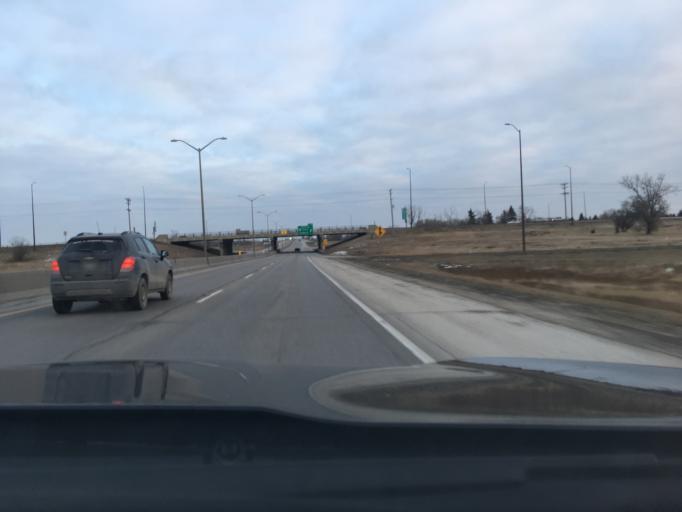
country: CA
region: Manitoba
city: Winnipeg
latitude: 49.9731
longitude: -97.0763
